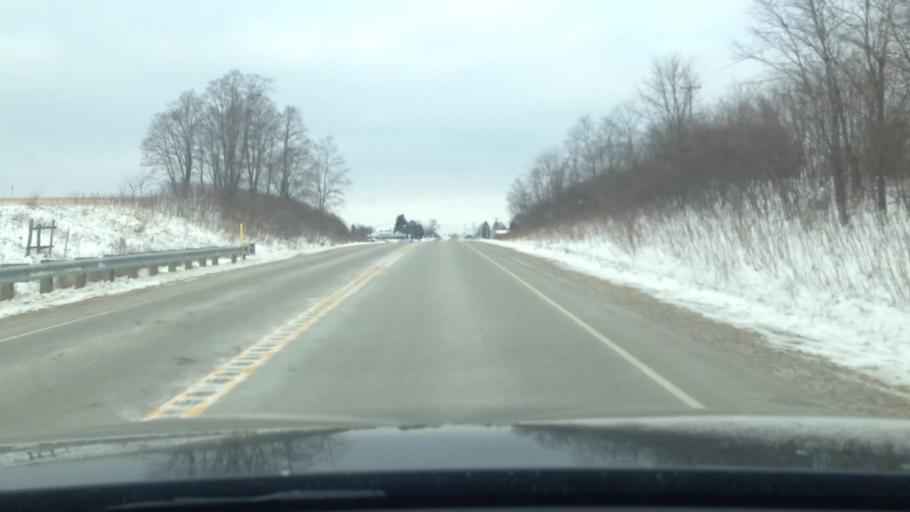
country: US
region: Wisconsin
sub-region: Walworth County
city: Lake Geneva
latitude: 42.5379
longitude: -88.4429
